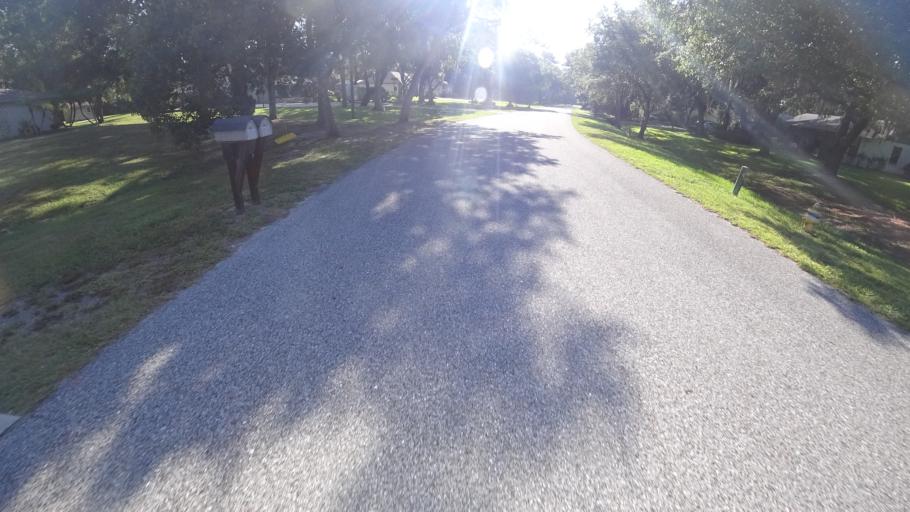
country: US
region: Florida
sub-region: Sarasota County
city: The Meadows
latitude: 27.4225
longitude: -82.4511
